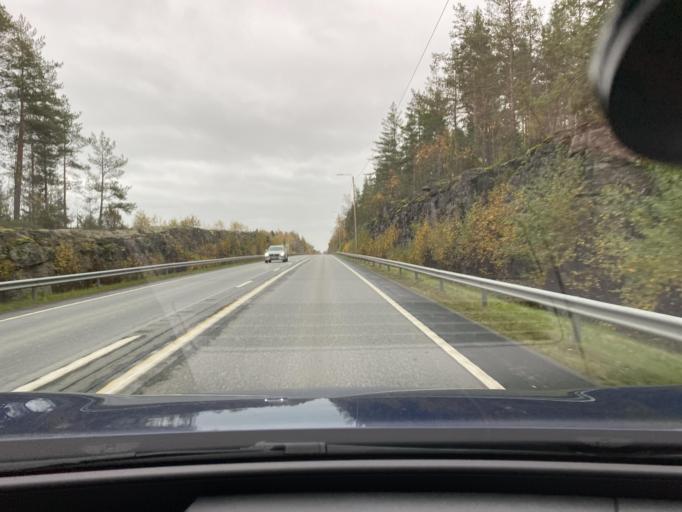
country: FI
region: Varsinais-Suomi
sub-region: Vakka-Suomi
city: Laitila
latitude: 60.9314
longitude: 21.6087
